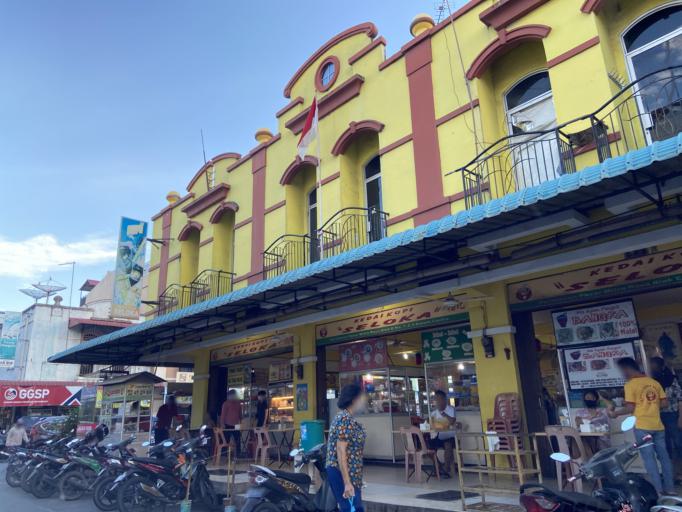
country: SG
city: Singapore
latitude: 1.1200
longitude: 104.0430
